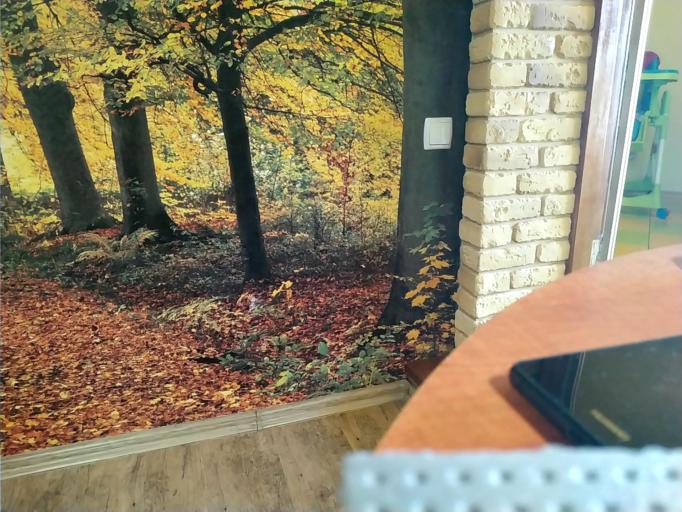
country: RU
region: Kaluga
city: Kondrovo
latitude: 54.7961
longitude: 35.9031
